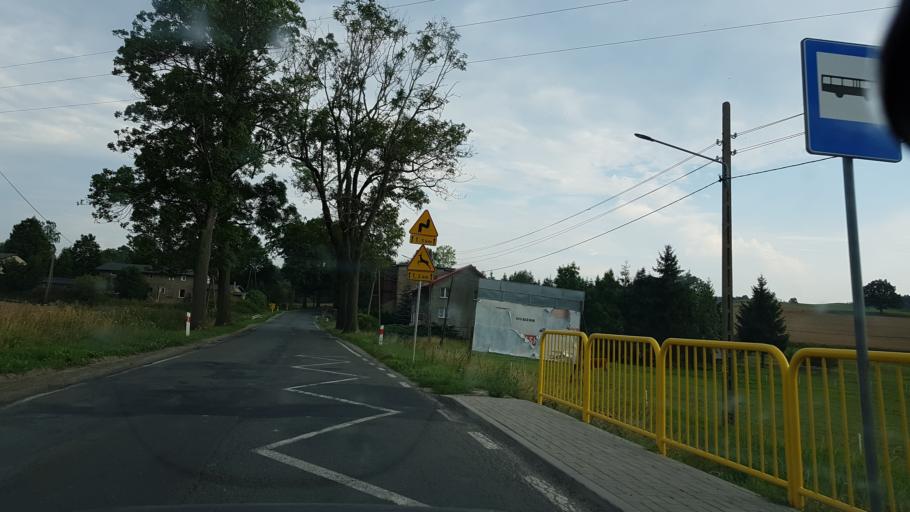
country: PL
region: Lower Silesian Voivodeship
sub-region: Powiat kamiennogorski
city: Marciszow
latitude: 50.8665
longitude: 15.9990
